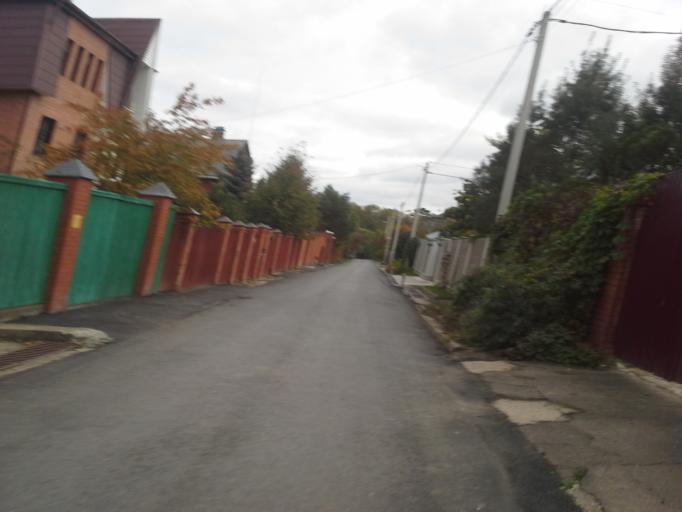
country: RU
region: Moskovskaya
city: Kokoshkino
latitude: 55.6185
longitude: 37.1629
